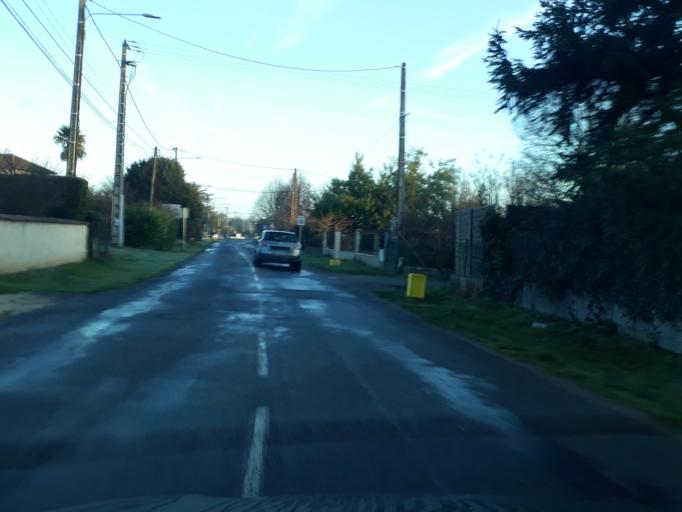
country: FR
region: Midi-Pyrenees
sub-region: Departement de la Haute-Garonne
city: Longages
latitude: 43.3481
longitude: 1.2367
